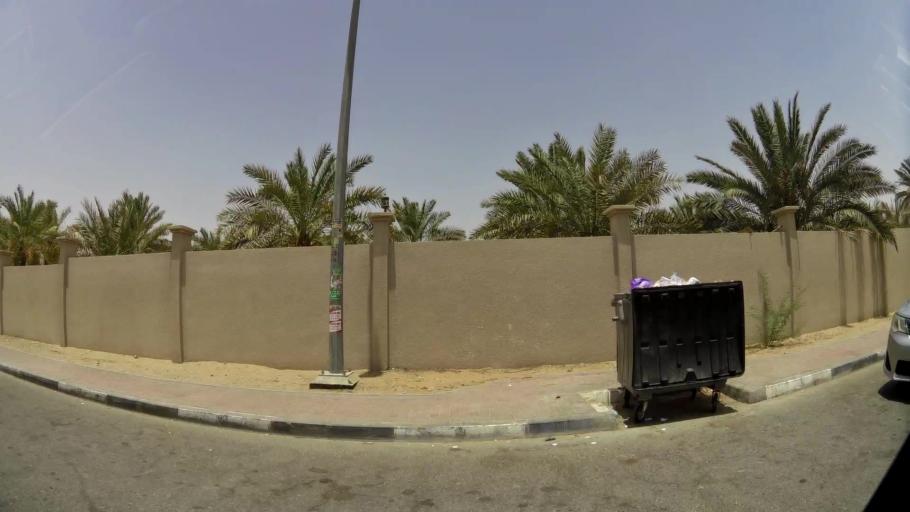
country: AE
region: Abu Dhabi
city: Al Ain
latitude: 24.1979
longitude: 55.7758
